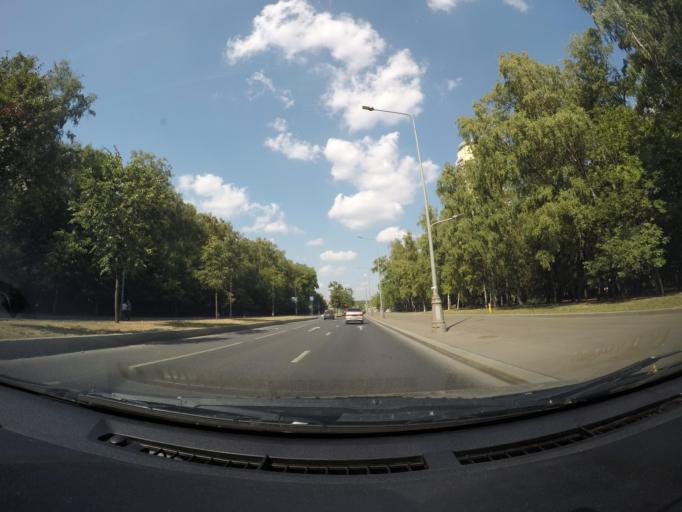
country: RU
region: Moskovskaya
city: Levoberezhnaya
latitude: 55.8745
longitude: 37.4827
